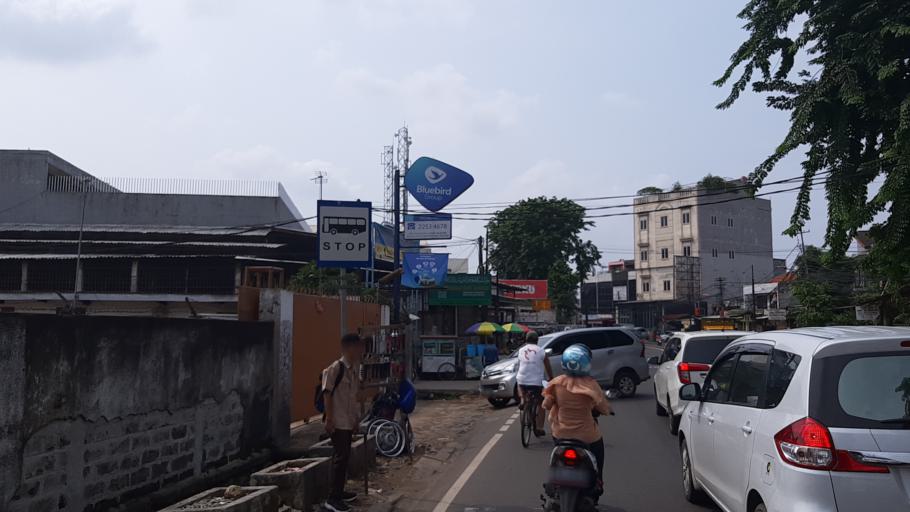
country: ID
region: Jakarta Raya
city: Jakarta
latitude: -6.2078
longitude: 106.7881
